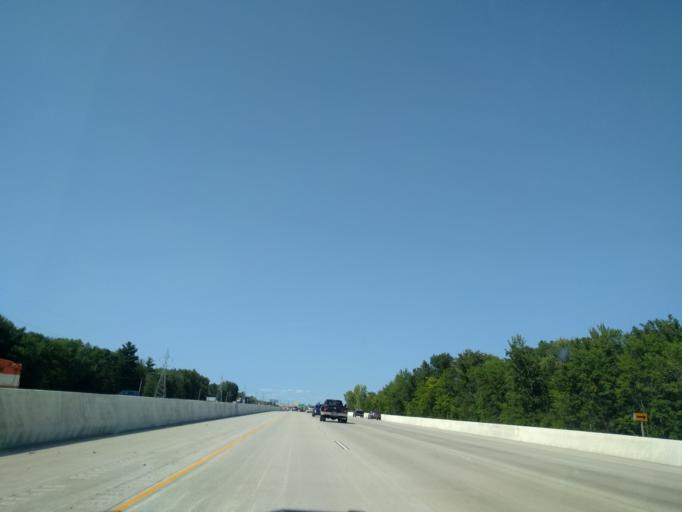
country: US
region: Wisconsin
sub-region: Brown County
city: Howard
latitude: 44.5783
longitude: -88.0485
